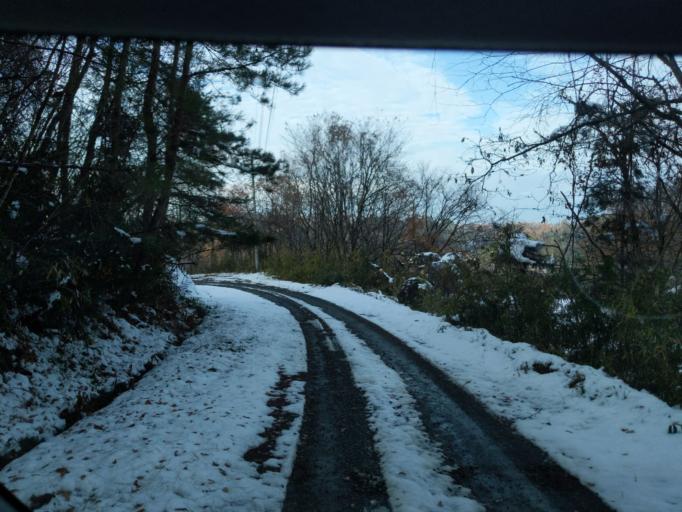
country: JP
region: Iwate
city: Mizusawa
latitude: 39.0398
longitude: 141.1032
